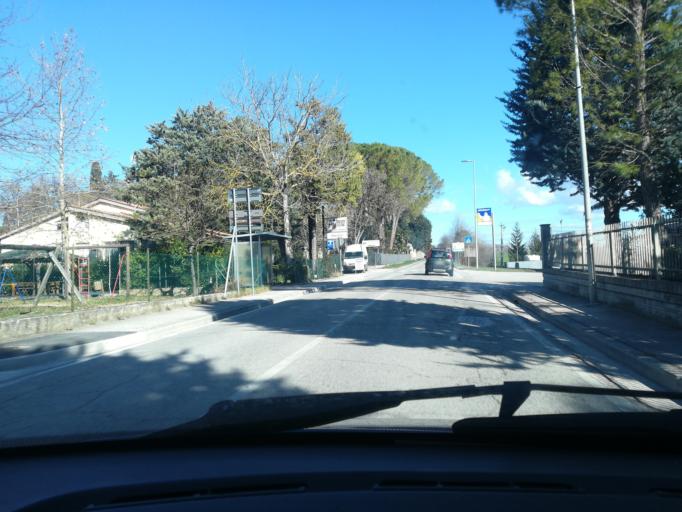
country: IT
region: The Marches
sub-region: Provincia di Macerata
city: Montecassiano
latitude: 43.3474
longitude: 13.4344
